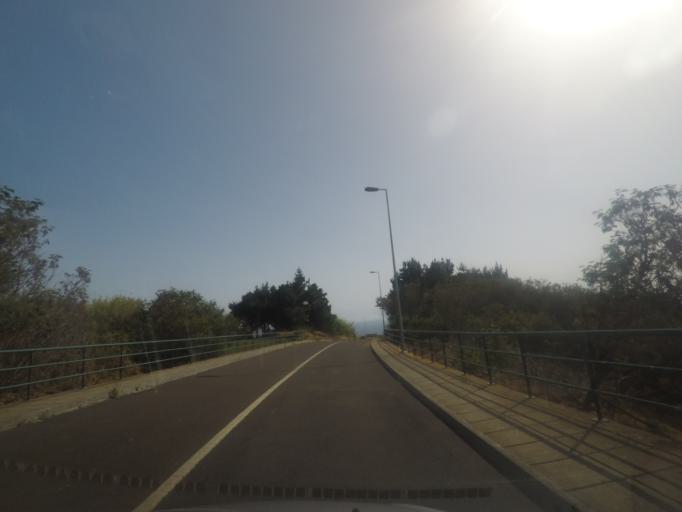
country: PT
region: Madeira
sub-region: Calheta
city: Faja da Ovelha
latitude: 32.8137
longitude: -17.2515
